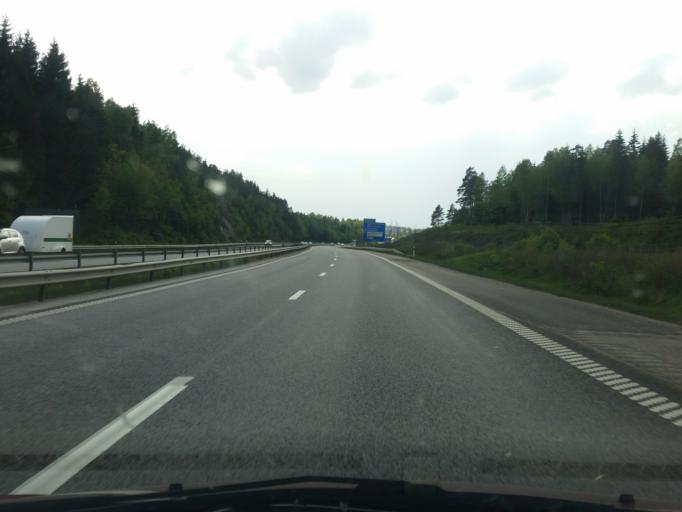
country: SE
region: Vaestra Goetaland
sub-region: Boras Kommun
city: Boras
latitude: 57.7131
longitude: 12.8896
